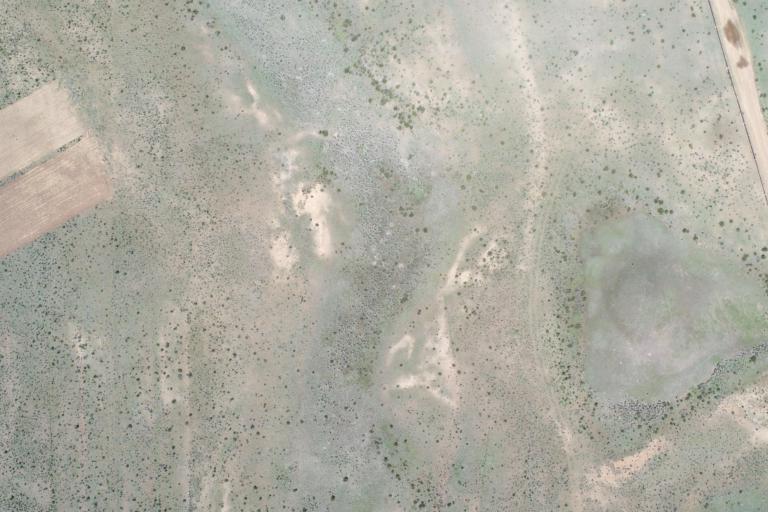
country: BO
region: La Paz
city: Curahuara de Carangas
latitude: -17.2799
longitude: -68.5145
